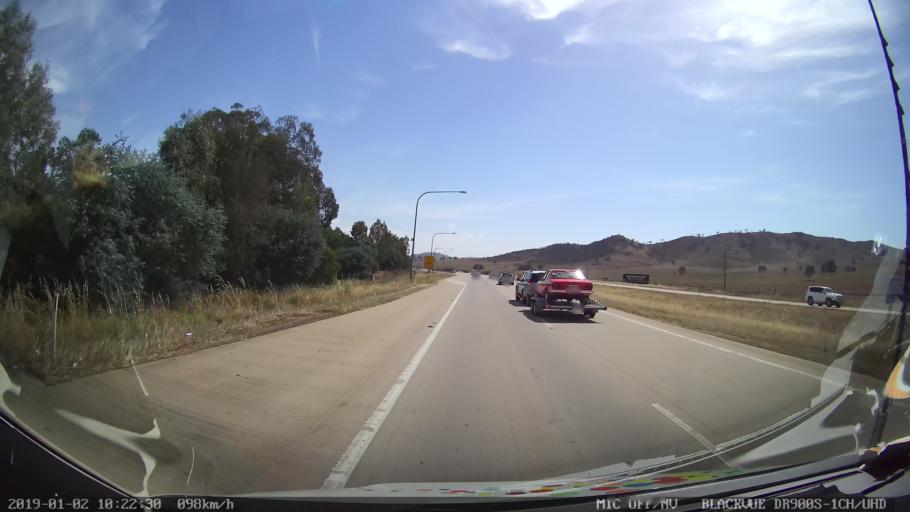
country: AU
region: New South Wales
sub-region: Gundagai
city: Gundagai
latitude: -34.9713
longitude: 148.1487
